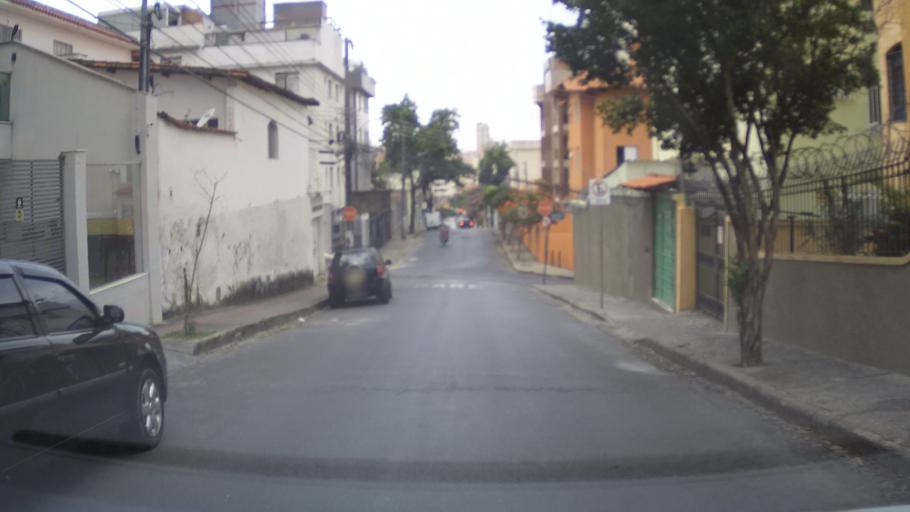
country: BR
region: Minas Gerais
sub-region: Belo Horizonte
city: Belo Horizonte
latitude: -19.9004
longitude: -43.9254
